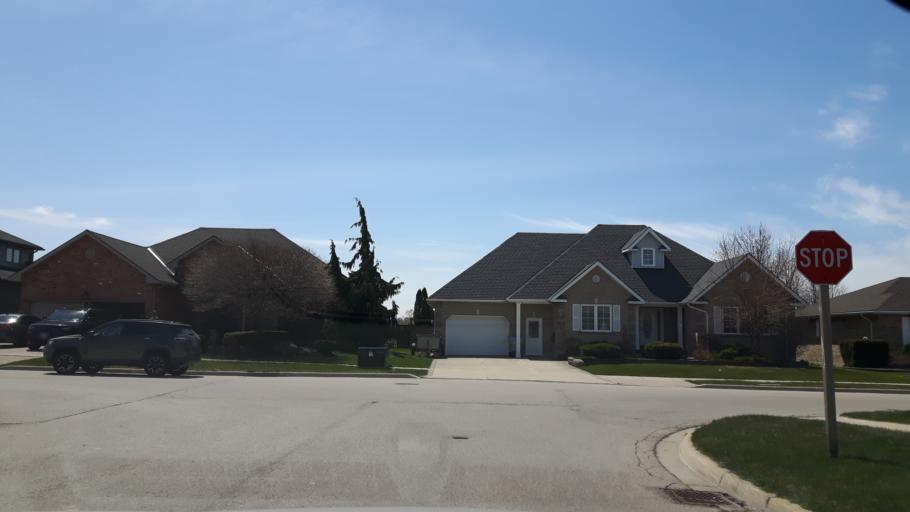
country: CA
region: Ontario
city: Goderich
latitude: 43.7287
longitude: -81.7198
